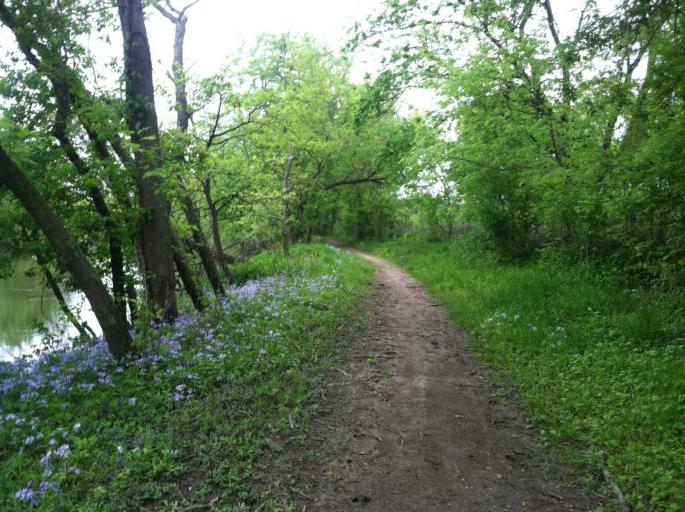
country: US
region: Illinois
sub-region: Cook County
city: River Grove
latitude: 41.9343
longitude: -87.8472
